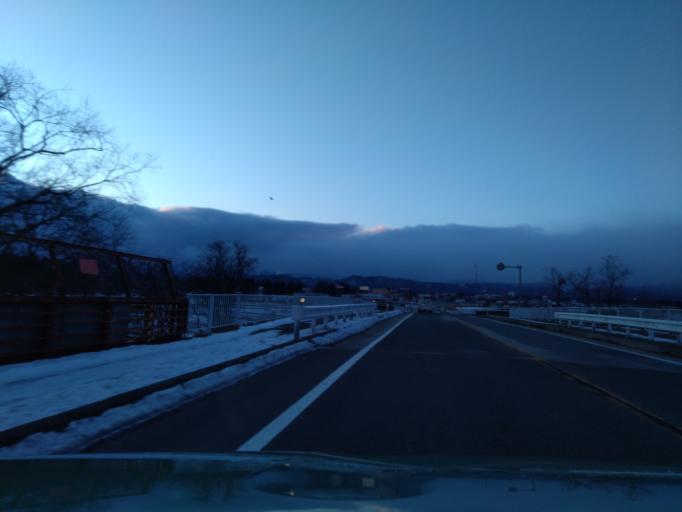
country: JP
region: Iwate
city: Shizukuishi
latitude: 39.6909
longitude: 140.9873
